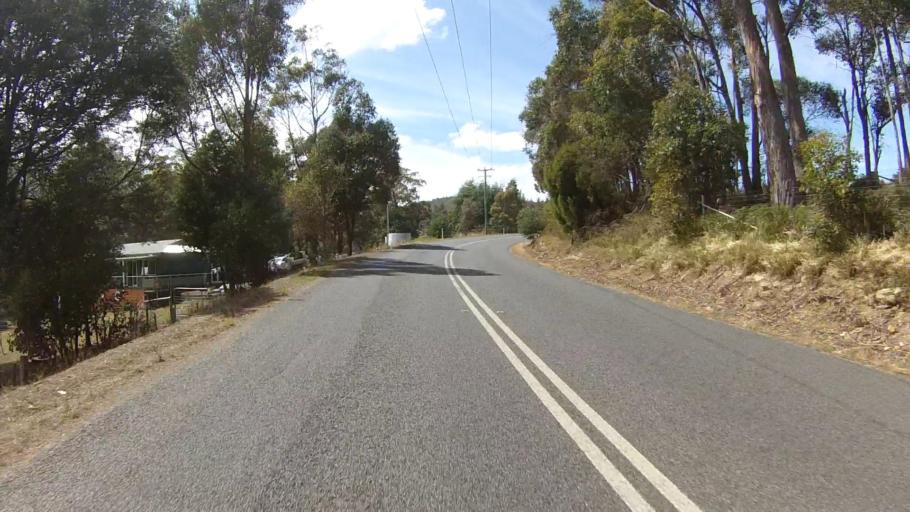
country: AU
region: Tasmania
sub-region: Huon Valley
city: Cygnet
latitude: -43.2141
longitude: 147.1188
